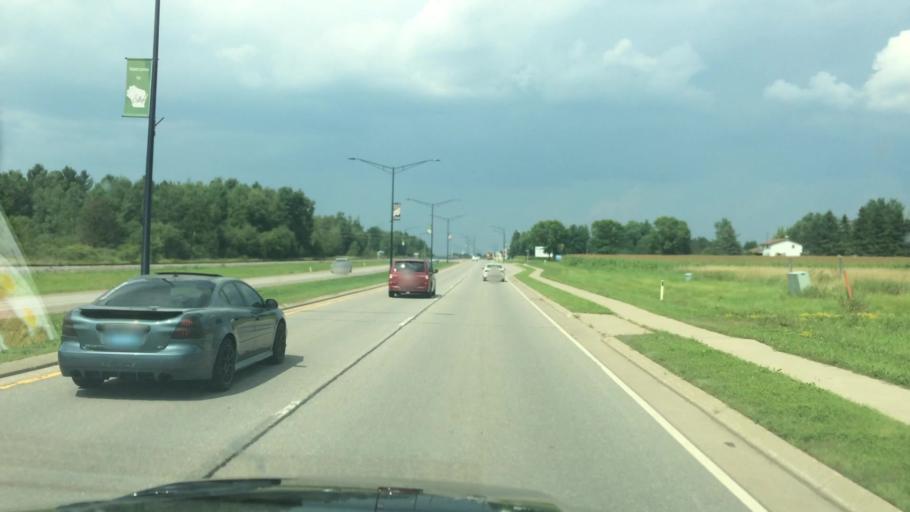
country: US
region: Wisconsin
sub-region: Clark County
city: Colby
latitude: 44.9210
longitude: -90.3155
